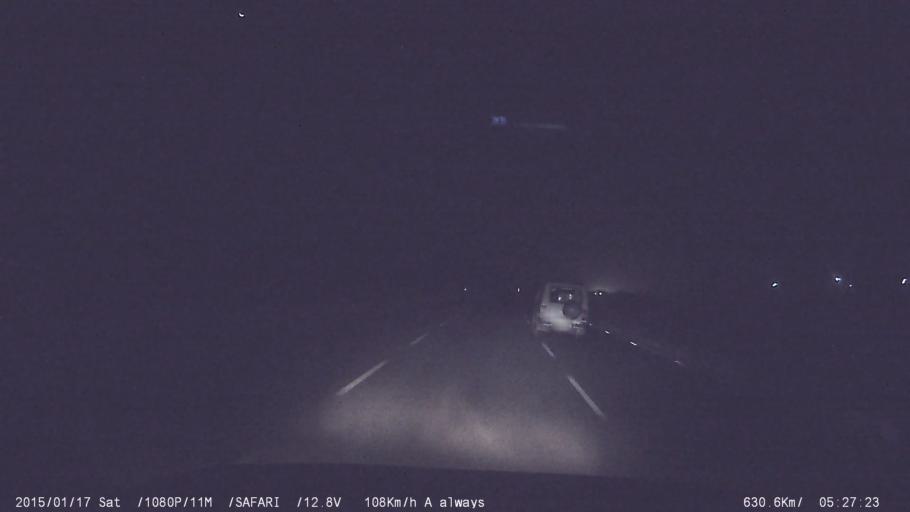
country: IN
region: Tamil Nadu
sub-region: Vellore
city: Arcot
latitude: 12.9340
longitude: 79.2602
